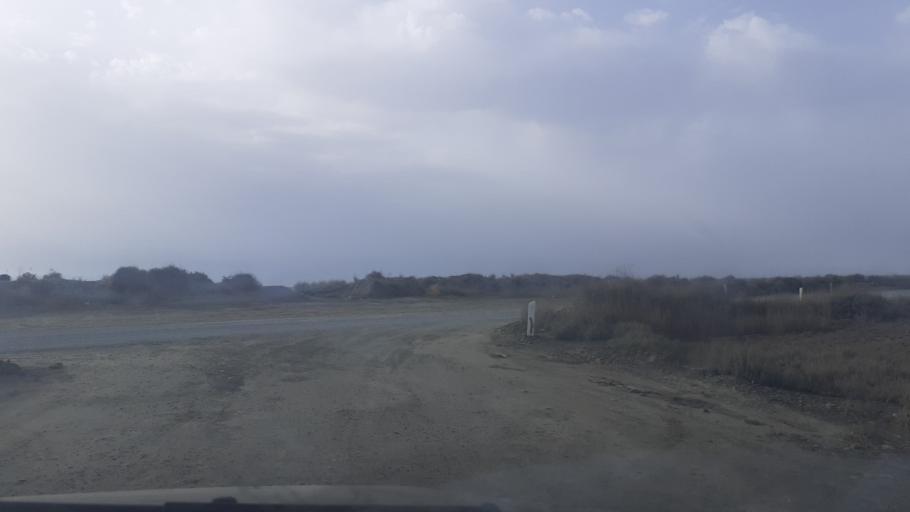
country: CY
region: Limassol
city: Limassol
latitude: 34.6318
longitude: 33.0070
